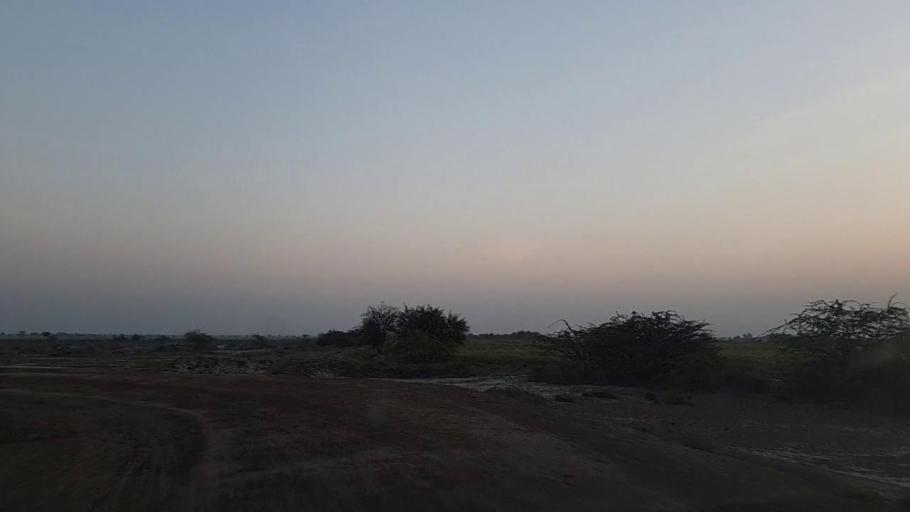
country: PK
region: Sindh
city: Naukot
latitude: 24.9954
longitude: 69.4334
